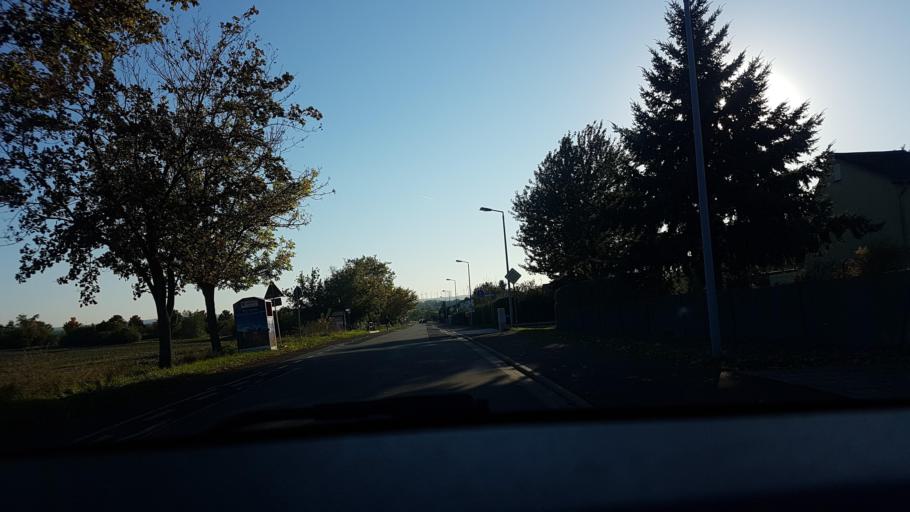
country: DE
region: Saxony-Anhalt
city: Bernburg
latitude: 51.7799
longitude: 11.7215
